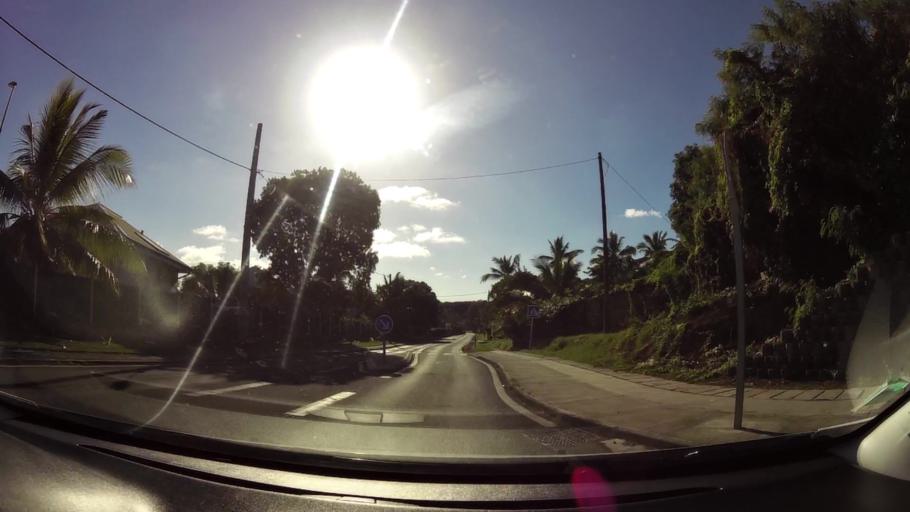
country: YT
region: Pamandzi
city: Pamandzi
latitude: -12.7948
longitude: 45.2728
